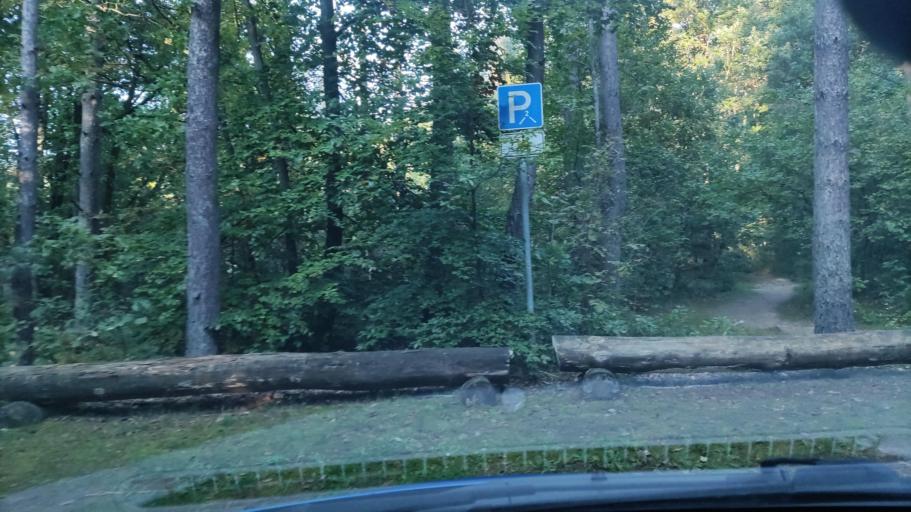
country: DE
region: Lower Saxony
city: Sudergellersen
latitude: 53.2168
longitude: 10.2750
